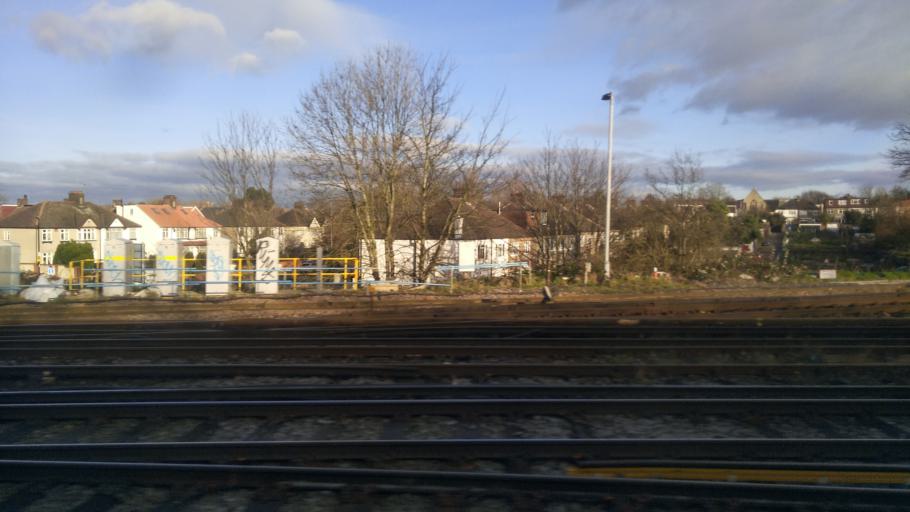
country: GB
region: England
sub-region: Greater London
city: Blackheath
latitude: 51.4450
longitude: 0.0060
